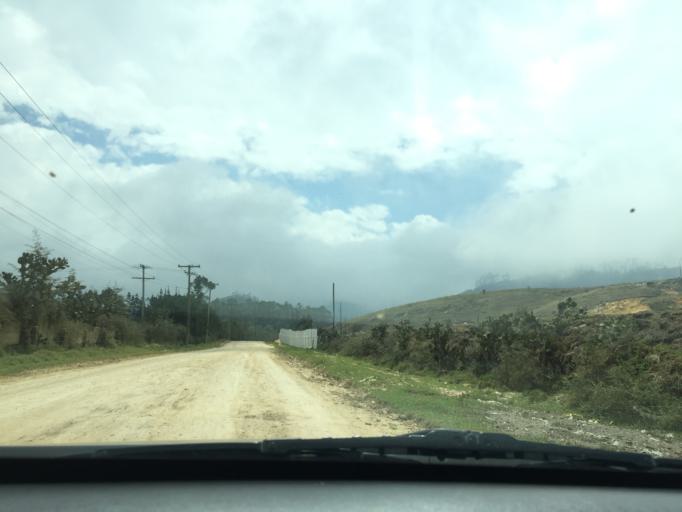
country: CO
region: Cundinamarca
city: Bojaca
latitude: 4.6989
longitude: -74.3119
